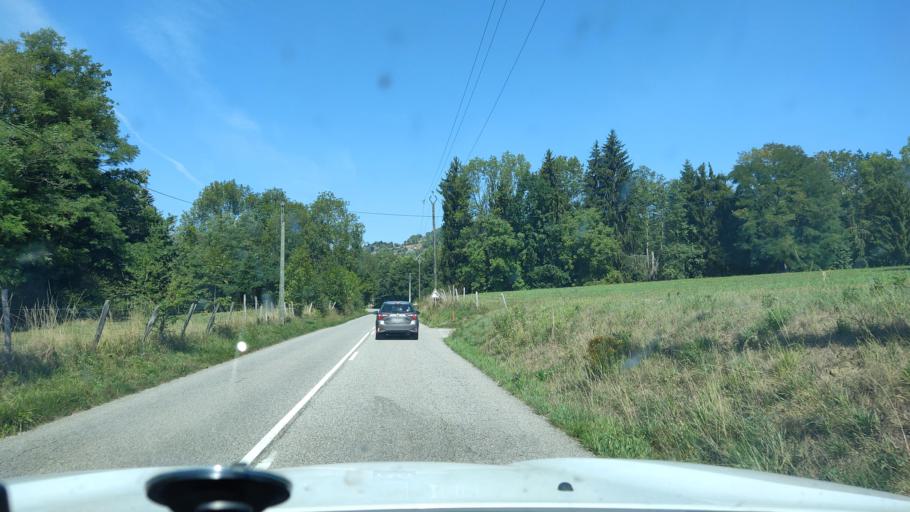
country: FR
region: Rhone-Alpes
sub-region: Departement de la Savoie
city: Novalaise
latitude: 45.5916
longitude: 5.7812
